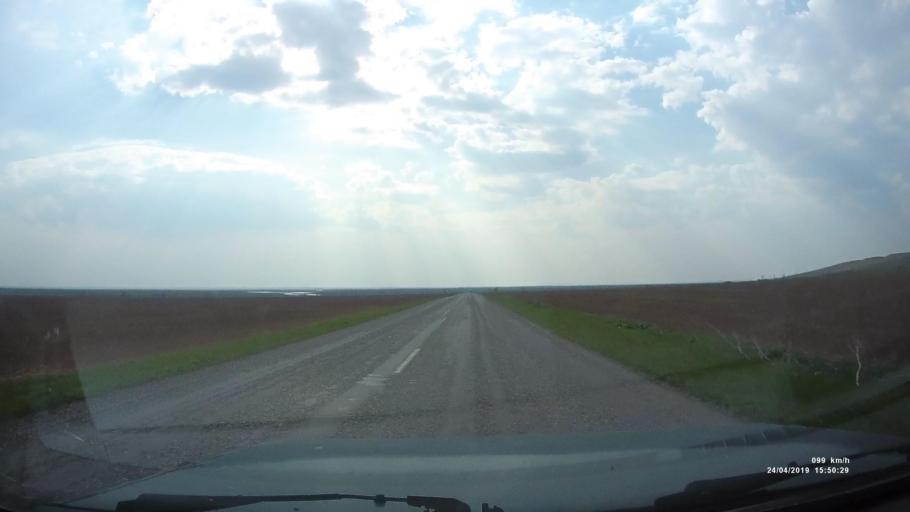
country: RU
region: Kalmykiya
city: Yashalta
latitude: 46.6041
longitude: 42.6320
